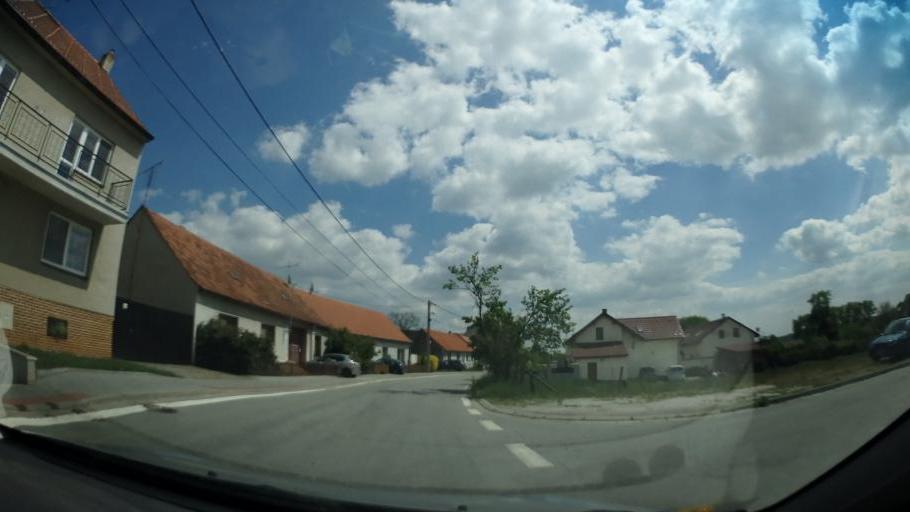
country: CZ
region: Vysocina
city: Hrotovice
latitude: 49.1288
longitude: 16.0831
